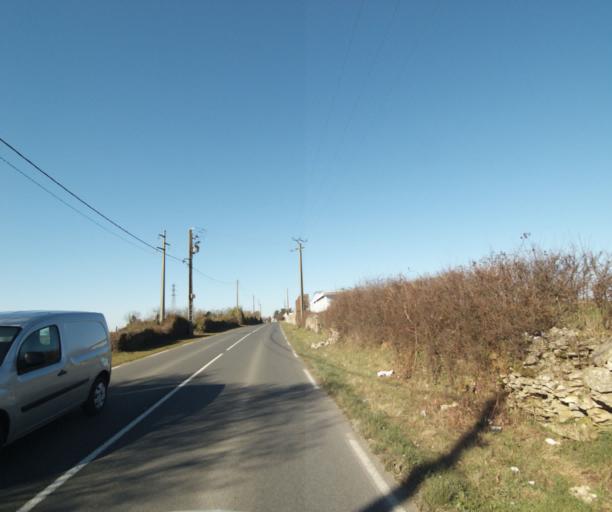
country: FR
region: Poitou-Charentes
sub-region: Departement des Deux-Sevres
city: Niort
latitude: 46.3544
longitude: -0.4802
